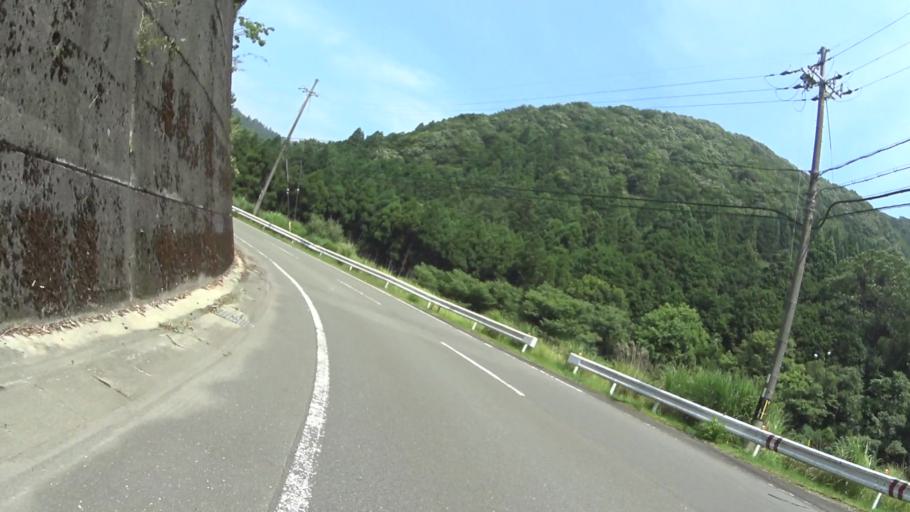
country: JP
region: Kyoto
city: Ayabe
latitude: 35.2952
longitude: 135.4275
